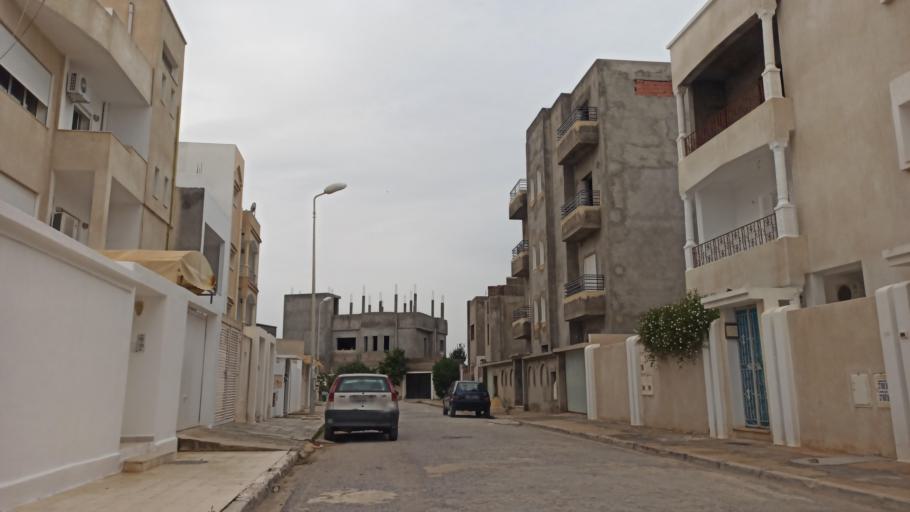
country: TN
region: Tunis
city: Hammam-Lif
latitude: 36.7102
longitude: 10.4140
